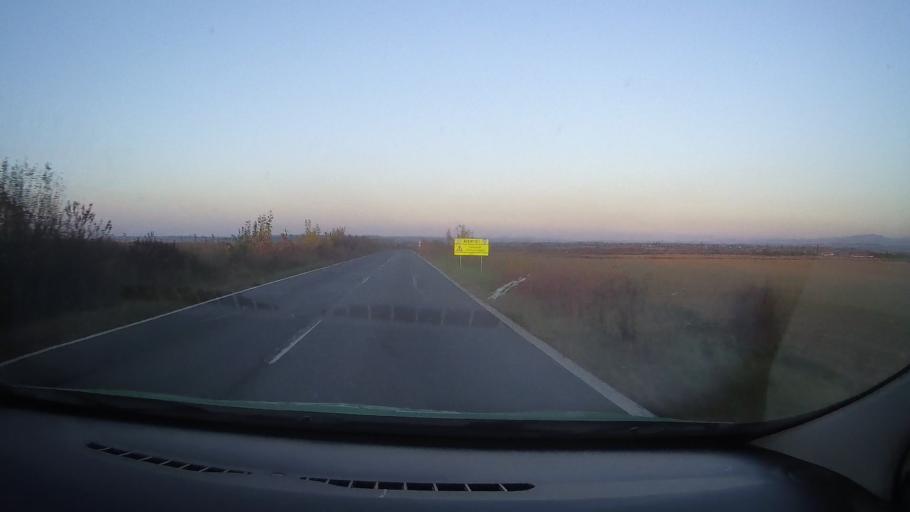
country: RO
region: Timis
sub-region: Comuna Manastiur
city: Manastiur
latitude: 45.8224
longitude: 22.0851
